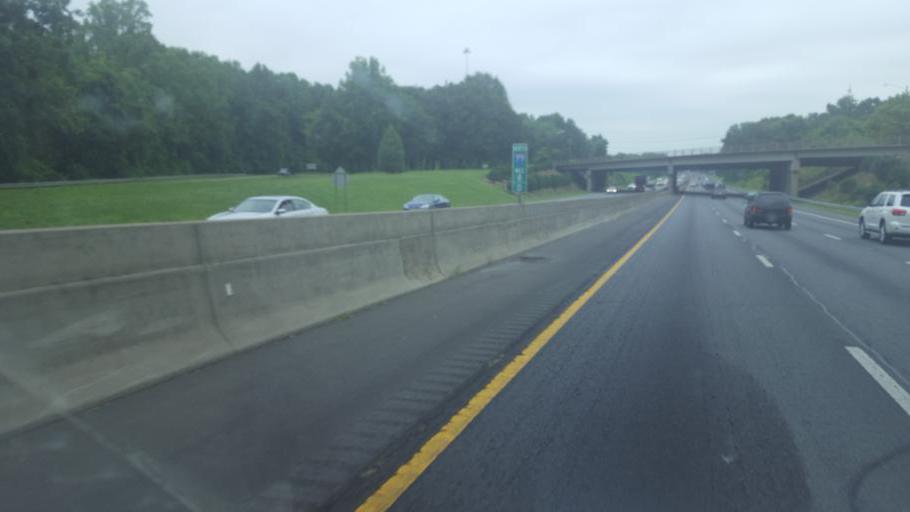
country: US
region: North Carolina
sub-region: Mecklenburg County
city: Charlotte
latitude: 35.2095
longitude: -80.8754
